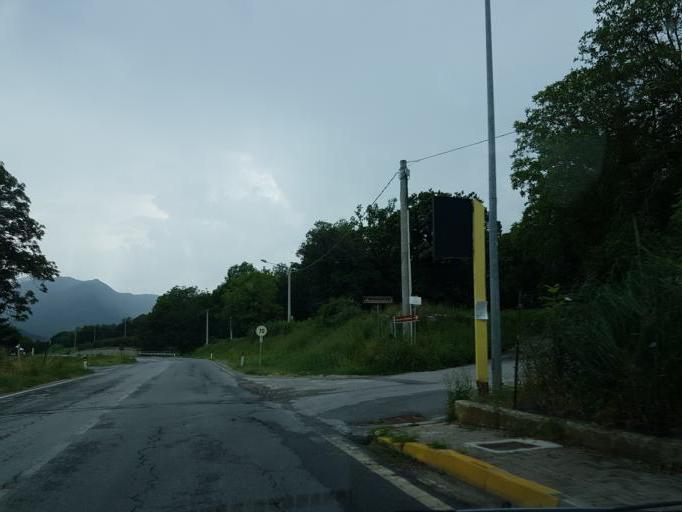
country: IT
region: Piedmont
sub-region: Provincia di Cuneo
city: Tettorosso
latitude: 44.4689
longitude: 7.3282
